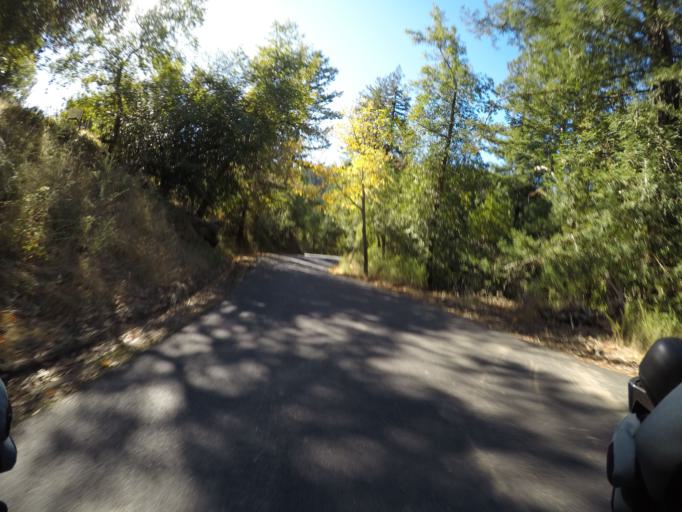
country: US
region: California
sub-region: Santa Clara County
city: Lexington Hills
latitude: 37.1580
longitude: -122.0146
